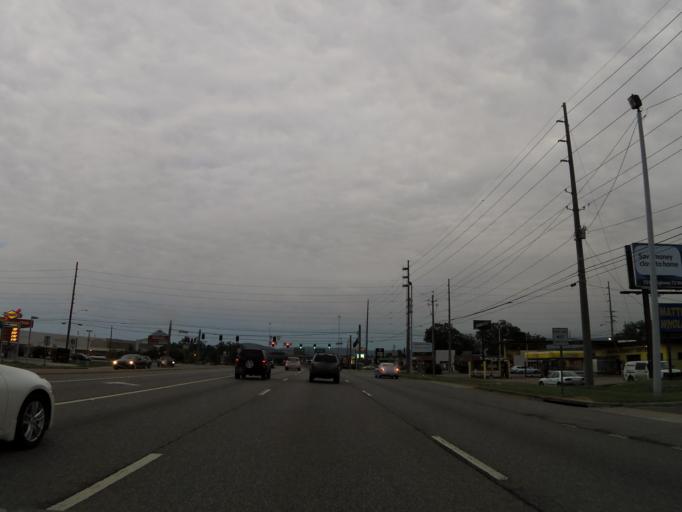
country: US
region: Alabama
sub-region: Madison County
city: Huntsville
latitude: 34.7384
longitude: -86.6043
